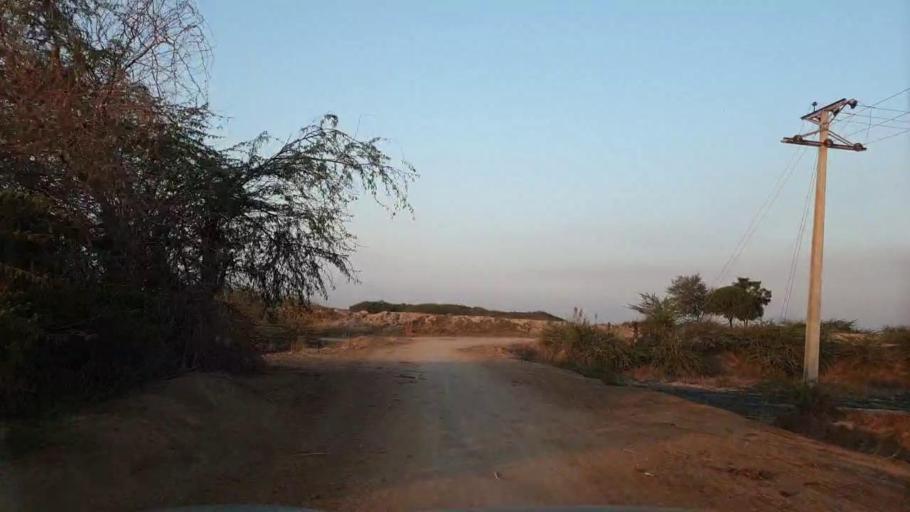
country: PK
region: Sindh
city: Berani
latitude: 25.6582
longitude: 68.7672
